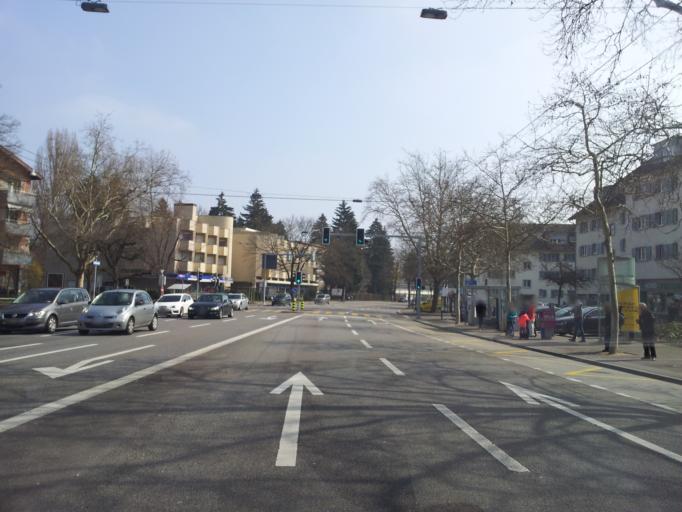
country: CH
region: Zurich
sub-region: Bezirk Zuerich
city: Zuerich (Kreis 11) / Affoltern
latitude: 47.4191
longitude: 8.5064
